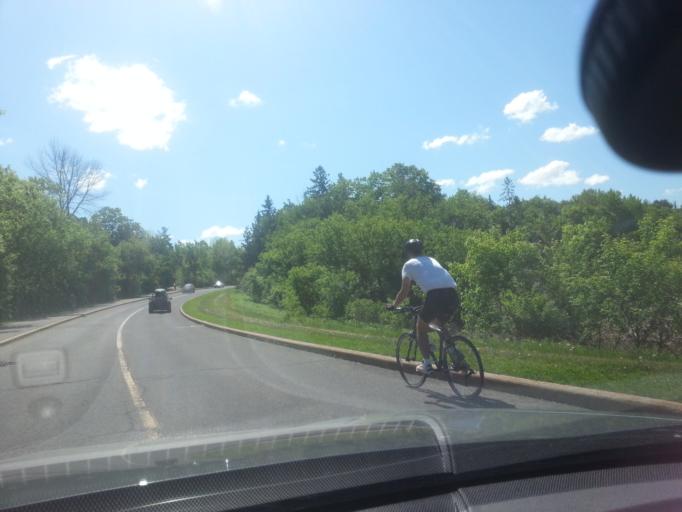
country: CA
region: Ontario
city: Ottawa
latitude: 45.4374
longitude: -75.7545
